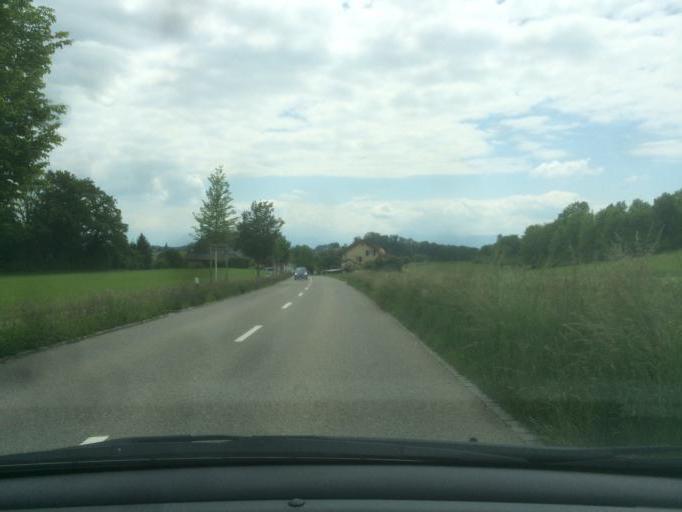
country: CH
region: Zurich
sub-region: Bezirk Hinwil
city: Wetzikon / Robenhausen
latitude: 47.3387
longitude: 8.7733
